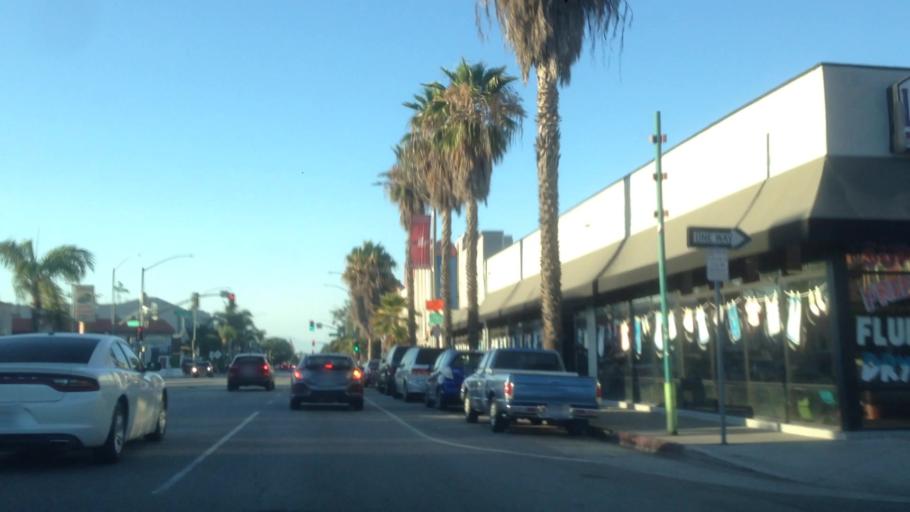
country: US
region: California
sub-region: Los Angeles County
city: Long Beach
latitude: 33.7698
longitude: -118.1819
